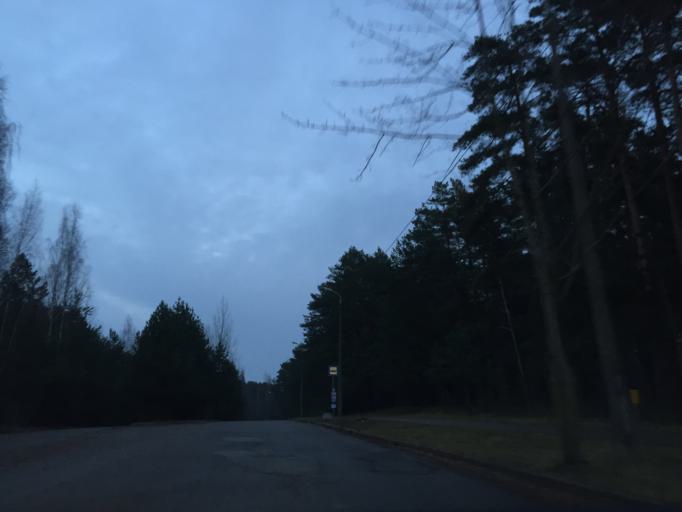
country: LV
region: Riga
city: Jaunciems
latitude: 57.0377
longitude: 24.1844
